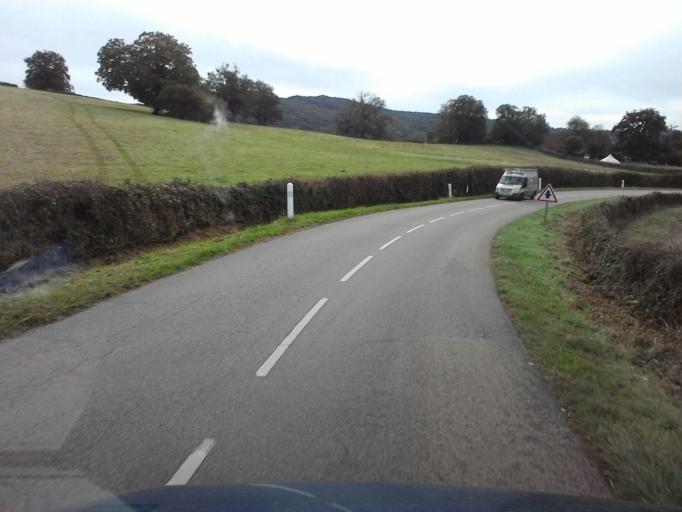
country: FR
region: Bourgogne
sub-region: Departement de la Nievre
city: Lormes
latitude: 47.2499
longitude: 3.8143
